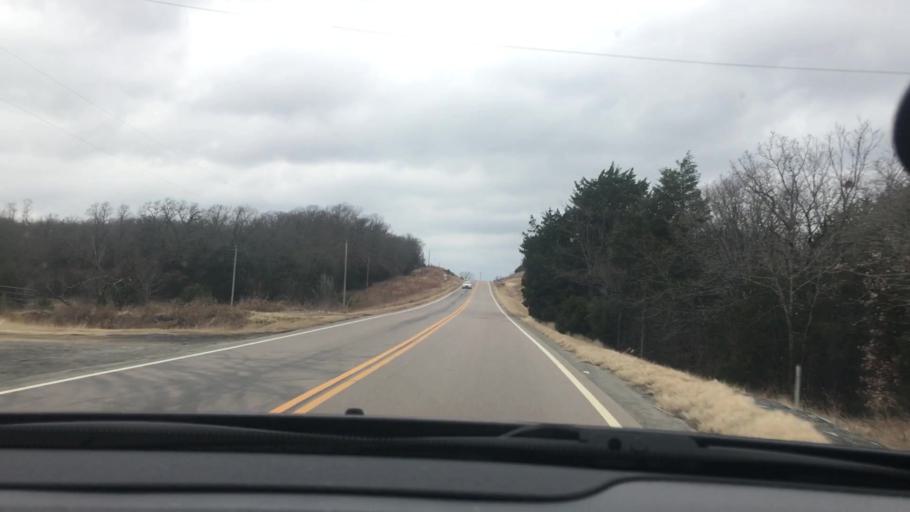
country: US
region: Oklahoma
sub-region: Coal County
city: Coalgate
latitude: 34.3749
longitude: -96.3929
